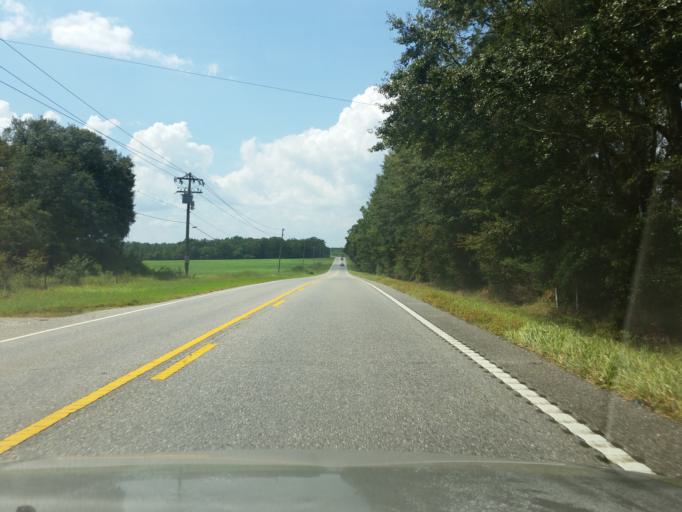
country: US
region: Alabama
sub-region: Baldwin County
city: Elberta
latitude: 30.5357
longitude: -87.5307
